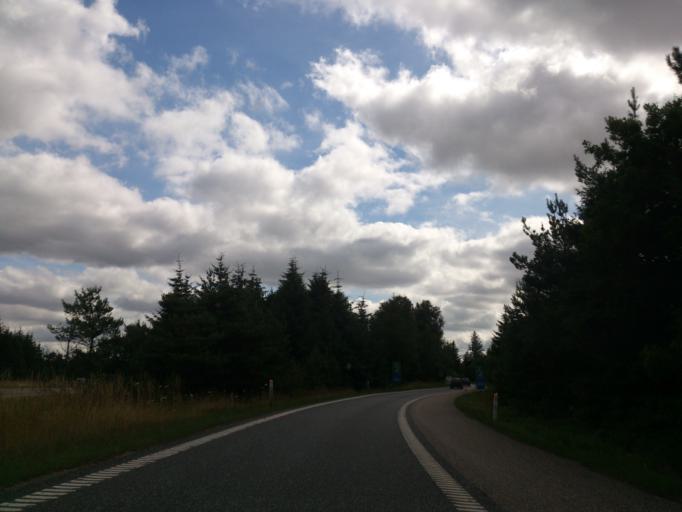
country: DK
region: South Denmark
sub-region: Aabenraa Kommune
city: Krusa
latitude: 54.8794
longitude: 9.3780
